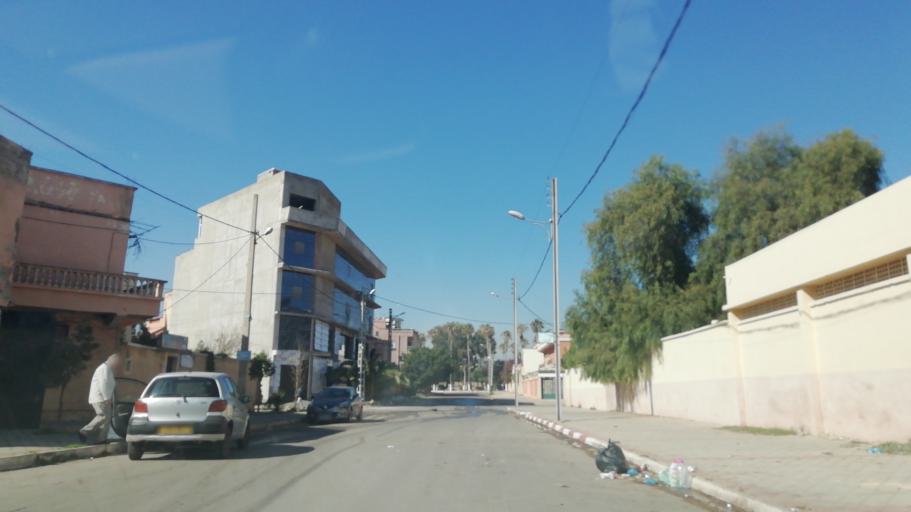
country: DZ
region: Oran
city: Oran
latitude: 35.6766
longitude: -0.6349
